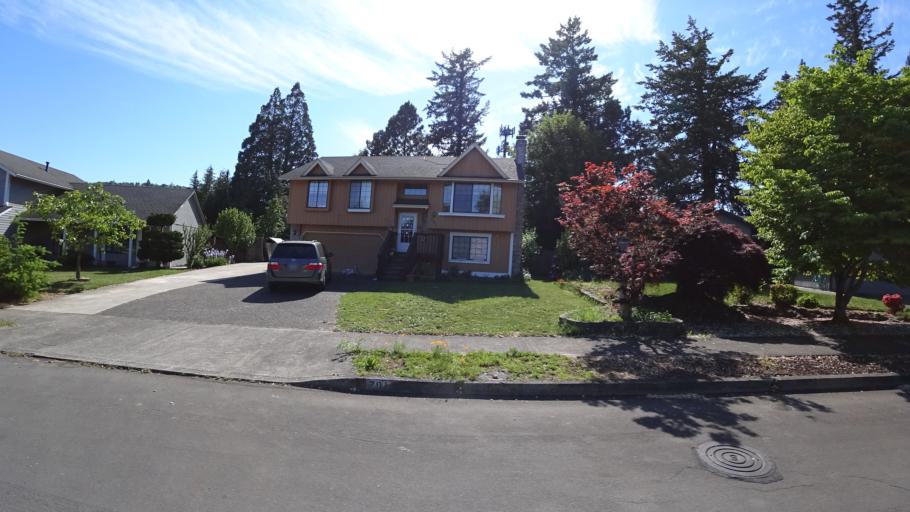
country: US
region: Oregon
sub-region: Multnomah County
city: Gresham
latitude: 45.4913
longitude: -122.4739
